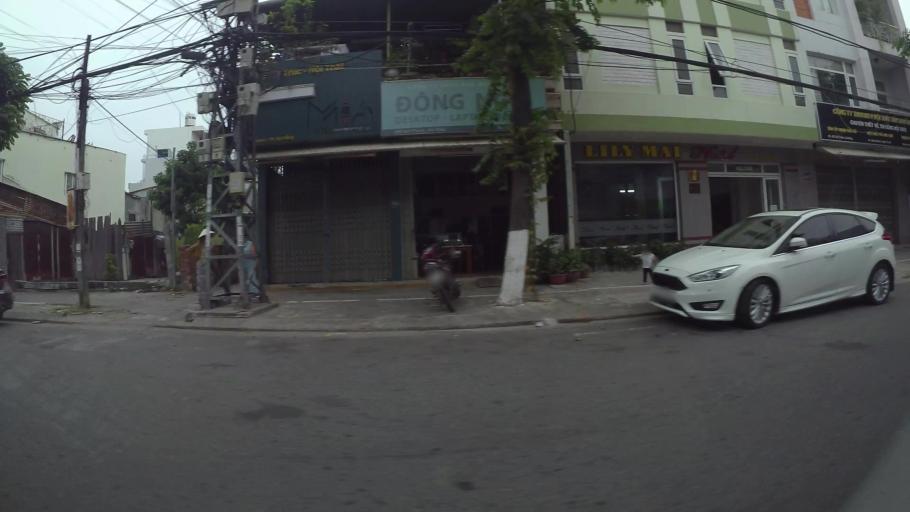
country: VN
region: Da Nang
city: Cam Le
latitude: 16.0298
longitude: 108.2226
